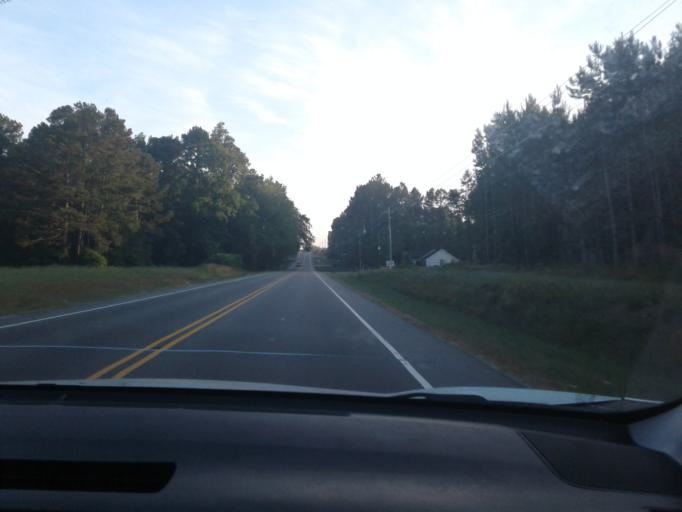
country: US
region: North Carolina
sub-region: Harnett County
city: Lillington
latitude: 35.4449
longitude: -78.8279
